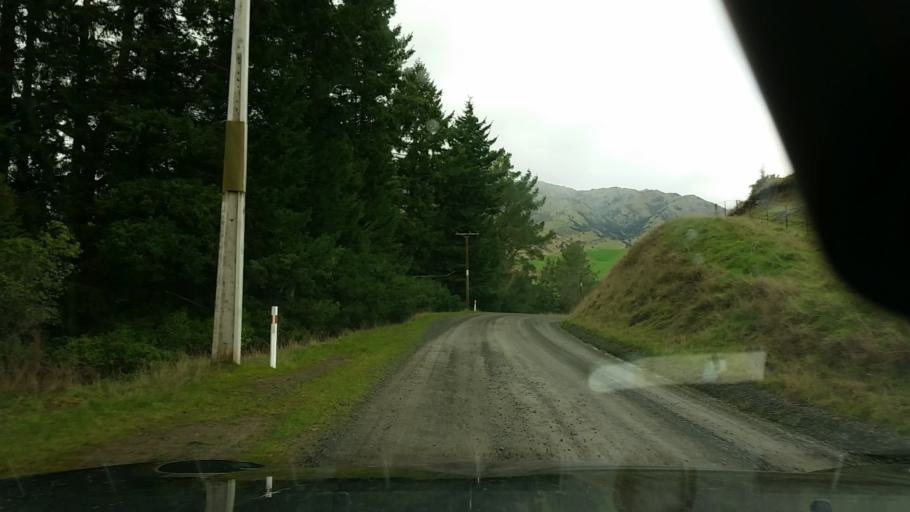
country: NZ
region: Marlborough
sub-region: Marlborough District
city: Blenheim
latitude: -41.6515
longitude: 173.6535
